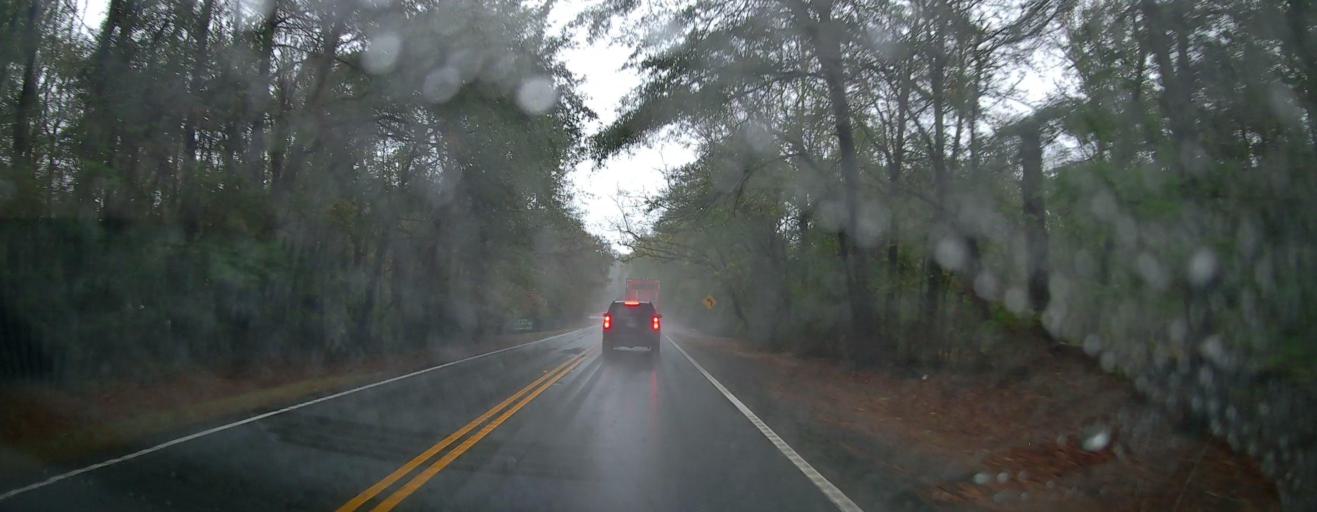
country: US
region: Georgia
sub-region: Jones County
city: Gray
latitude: 33.1348
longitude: -83.4683
